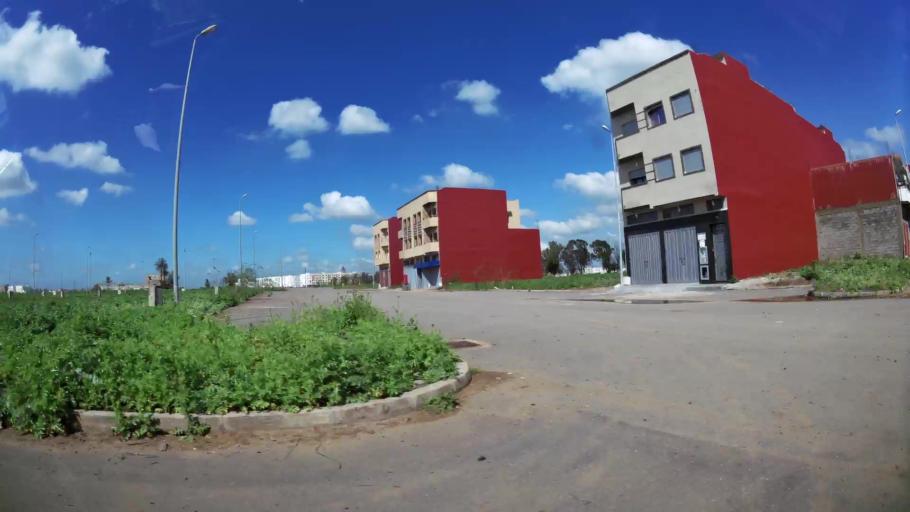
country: MA
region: Grand Casablanca
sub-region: Mediouna
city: Mediouna
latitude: 33.4485
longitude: -7.5031
